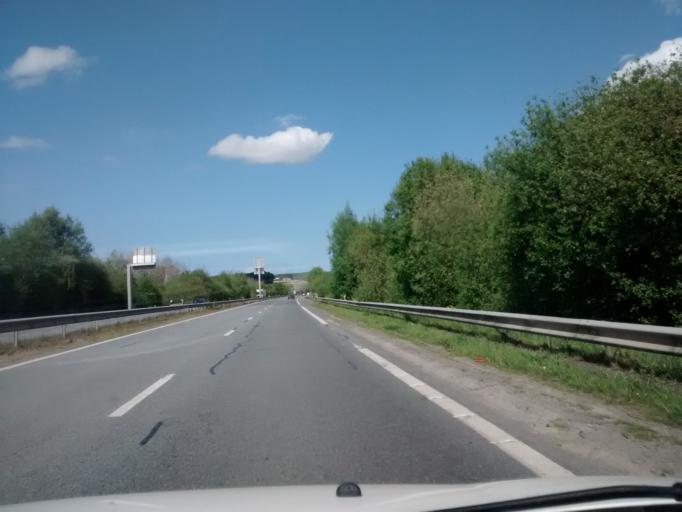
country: FR
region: Brittany
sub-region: Departement des Cotes-d'Armor
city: Saint-Samson-sur-Rance
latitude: 48.4914
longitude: -2.0412
